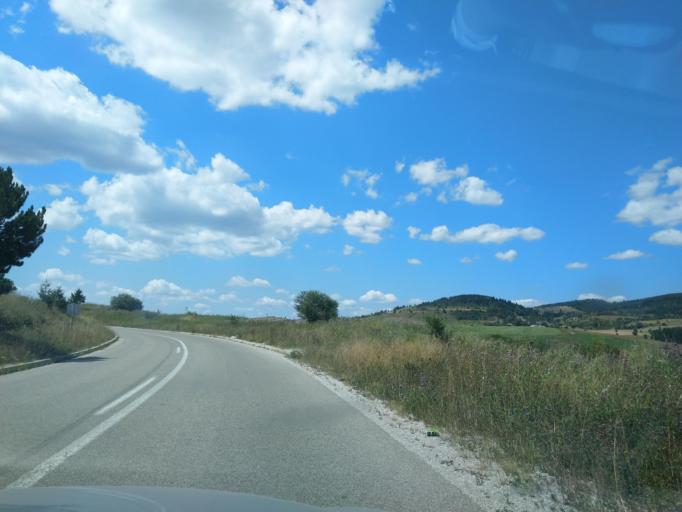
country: RS
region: Central Serbia
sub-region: Zlatiborski Okrug
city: Sjenica
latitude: 43.3302
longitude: 19.8753
